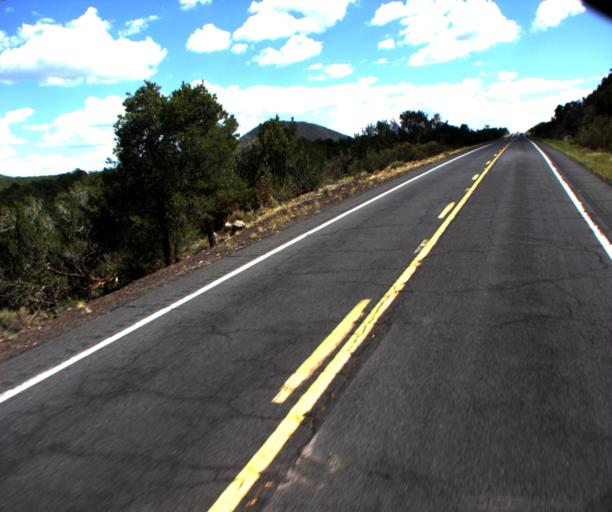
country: US
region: Arizona
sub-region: Coconino County
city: Williams
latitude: 35.4240
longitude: -112.1707
